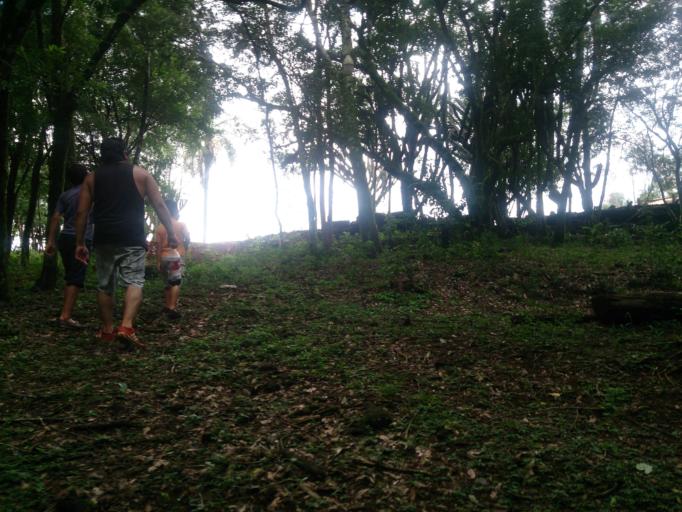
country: AR
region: Misiones
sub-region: Departamento de Obera
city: Obera
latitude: -27.5117
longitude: -55.1064
